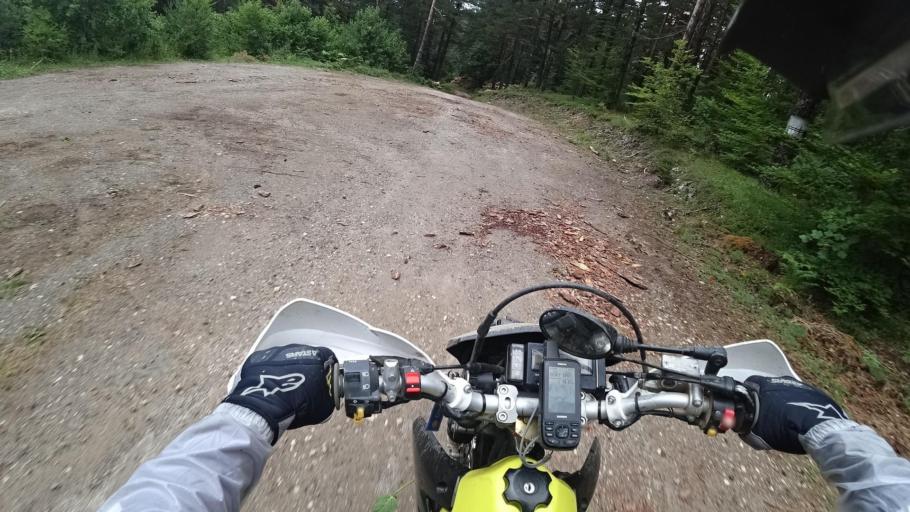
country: HR
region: Licko-Senjska
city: Otocac
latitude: 44.8700
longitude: 15.4017
